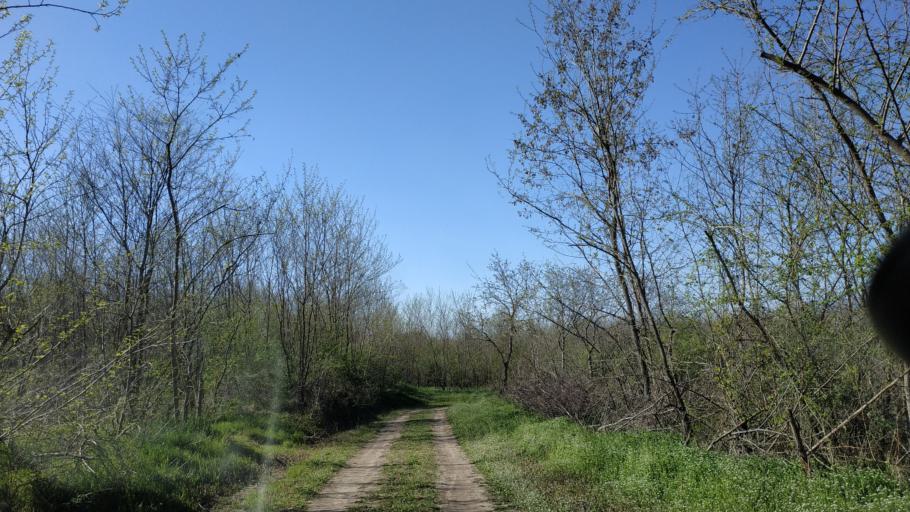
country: RS
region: Central Serbia
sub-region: Nisavski Okrug
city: Aleksinac
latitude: 43.4889
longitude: 21.6835
